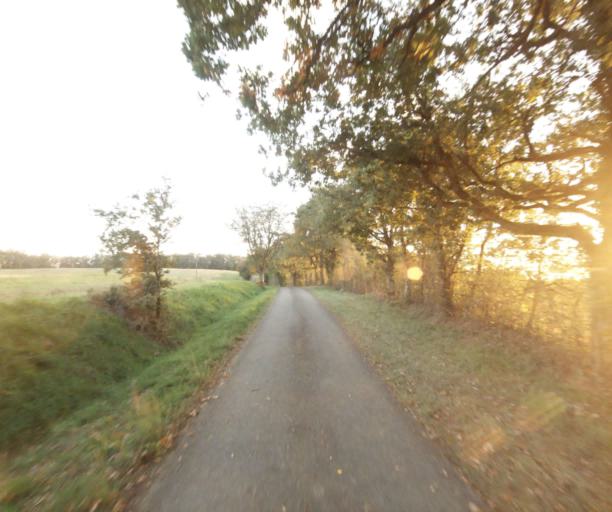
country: FR
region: Midi-Pyrenees
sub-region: Departement du Gers
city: Vic-Fezensac
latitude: 43.7764
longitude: 0.2007
